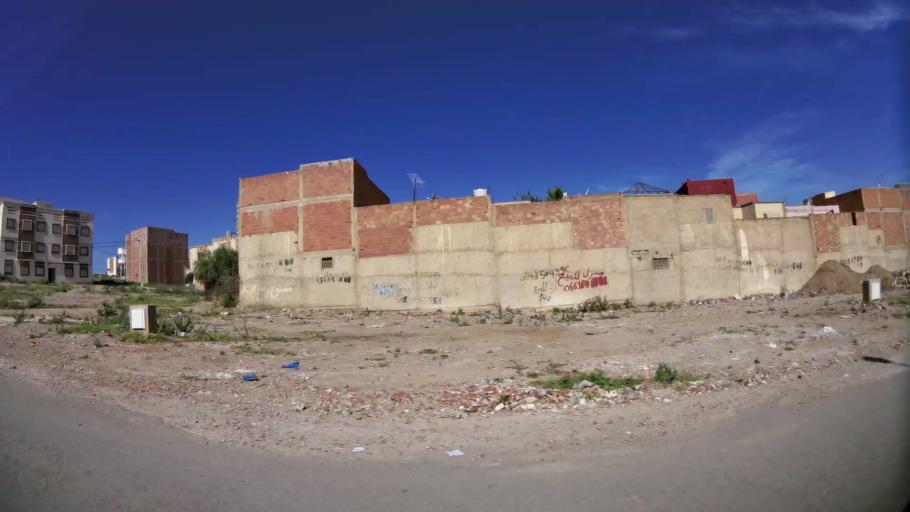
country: MA
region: Oriental
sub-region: Oujda-Angad
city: Oujda
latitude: 34.6564
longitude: -1.9418
